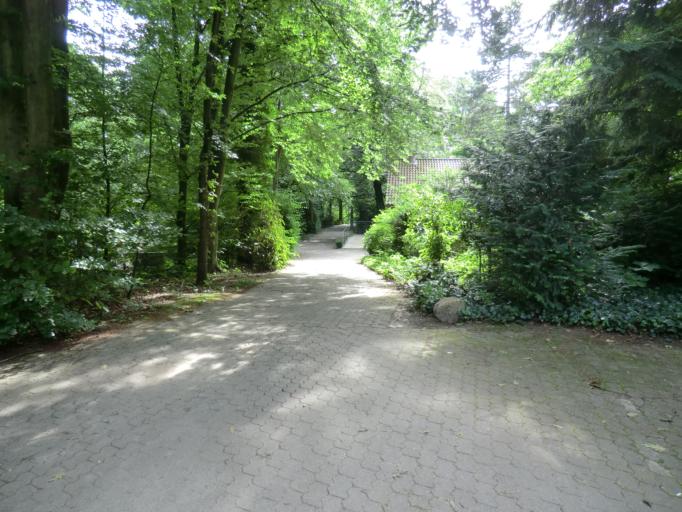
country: DE
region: North Rhine-Westphalia
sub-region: Regierungsbezirk Detmold
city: Herford
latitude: 52.1372
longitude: 8.6888
